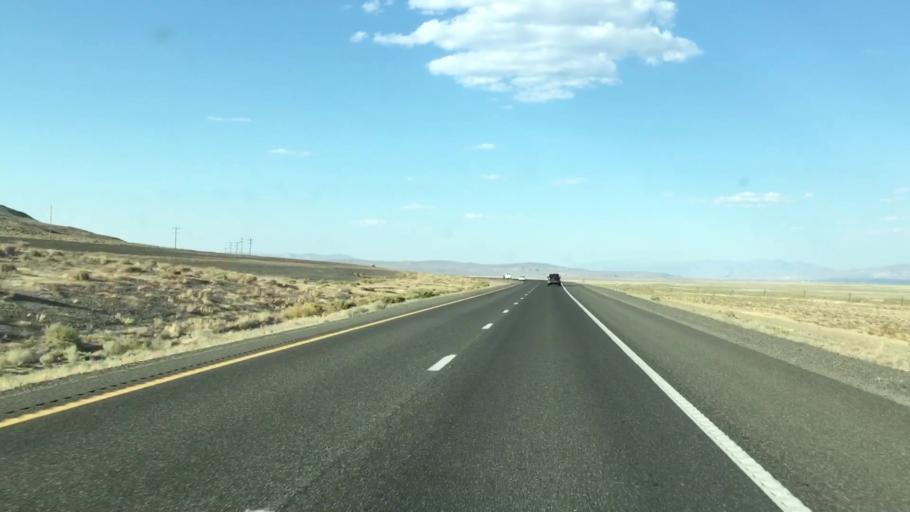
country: US
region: Nevada
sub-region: Pershing County
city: Lovelock
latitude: 39.9854
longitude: -118.6866
